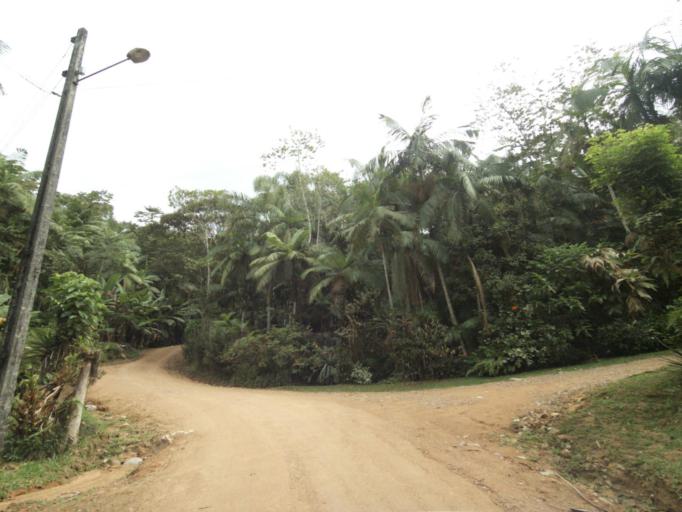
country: BR
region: Santa Catarina
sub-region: Pomerode
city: Pomerode
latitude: -26.7361
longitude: -49.1989
